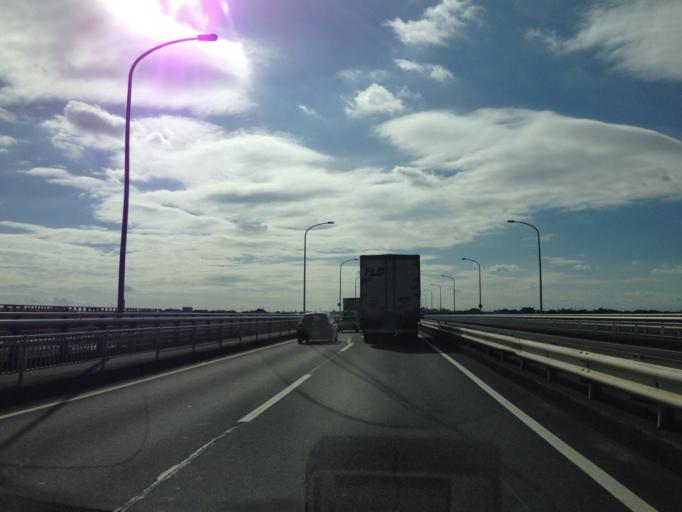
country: JP
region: Ibaraki
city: Toride
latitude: 35.8933
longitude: 140.0578
